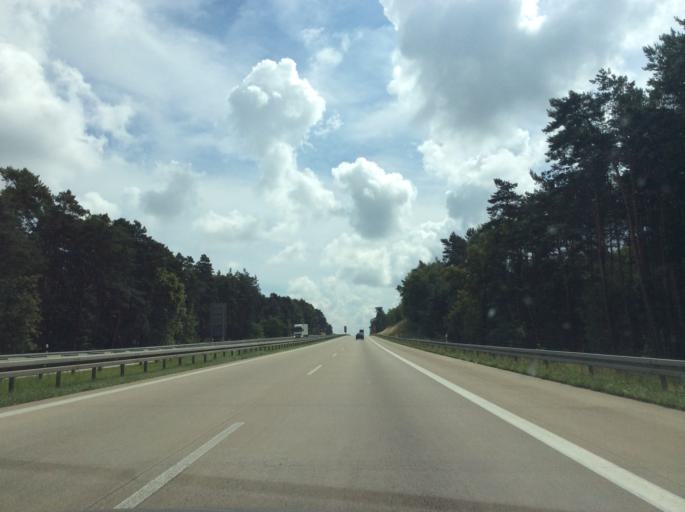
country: DE
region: Brandenburg
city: Jacobsdorf
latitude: 52.3202
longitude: 14.4078
